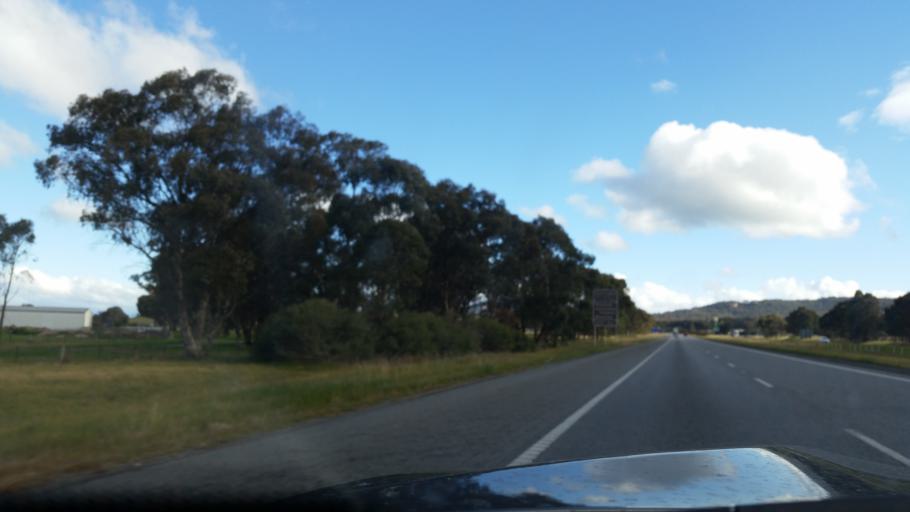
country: AU
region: Victoria
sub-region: Wangaratta
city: Wangaratta
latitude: -36.4333
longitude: 146.2551
